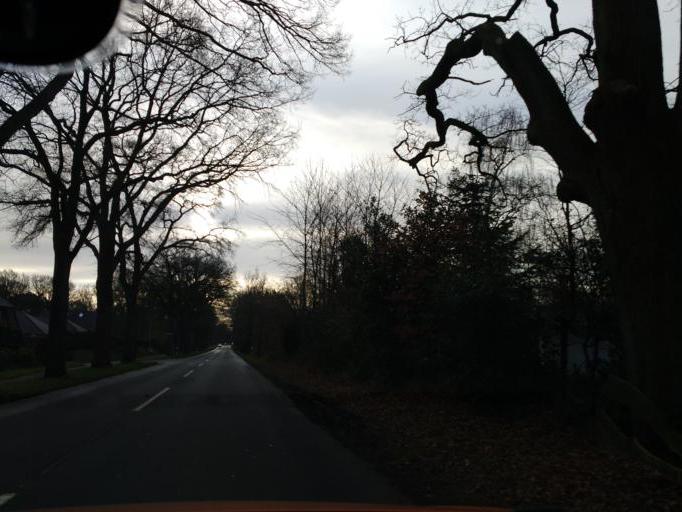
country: DE
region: Lower Saxony
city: Hude
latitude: 53.1023
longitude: 8.4535
